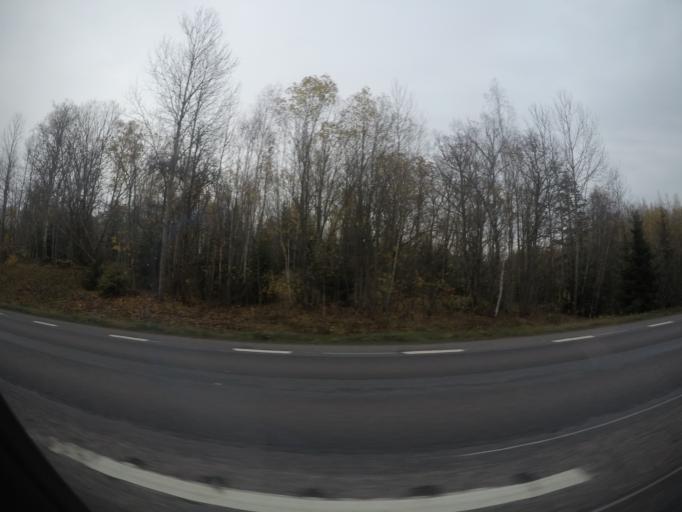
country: SE
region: Soedermanland
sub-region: Eskilstuna Kommun
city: Kvicksund
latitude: 59.4765
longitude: 16.3053
